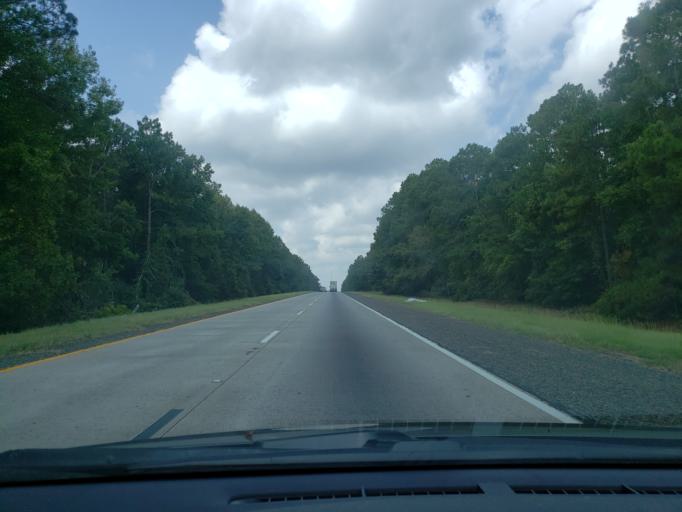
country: US
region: Georgia
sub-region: Treutlen County
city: Soperton
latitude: 32.4348
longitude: -82.6400
